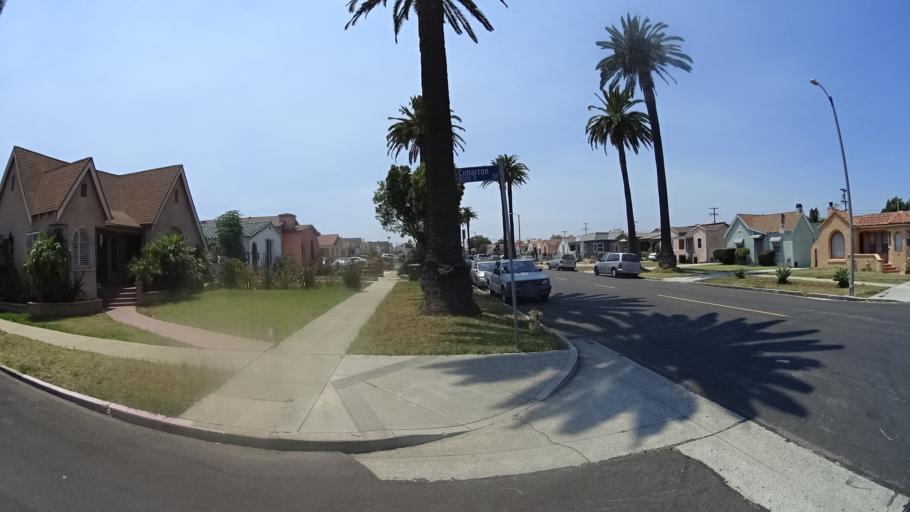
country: US
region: California
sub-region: Los Angeles County
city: Westmont
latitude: 33.9636
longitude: -118.3156
